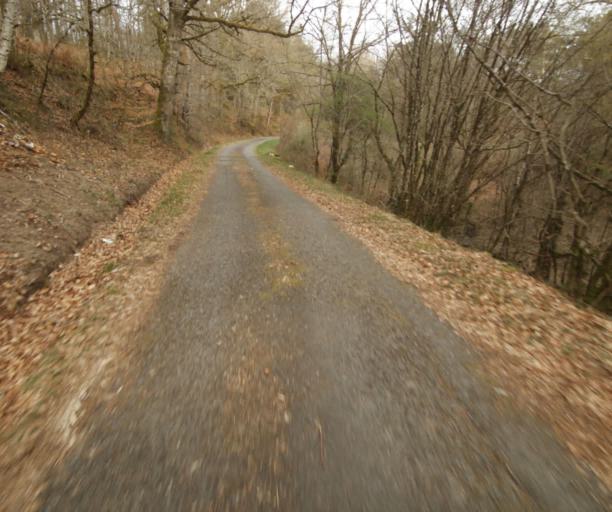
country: FR
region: Limousin
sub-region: Departement de la Correze
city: Argentat
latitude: 45.2076
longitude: 1.9917
